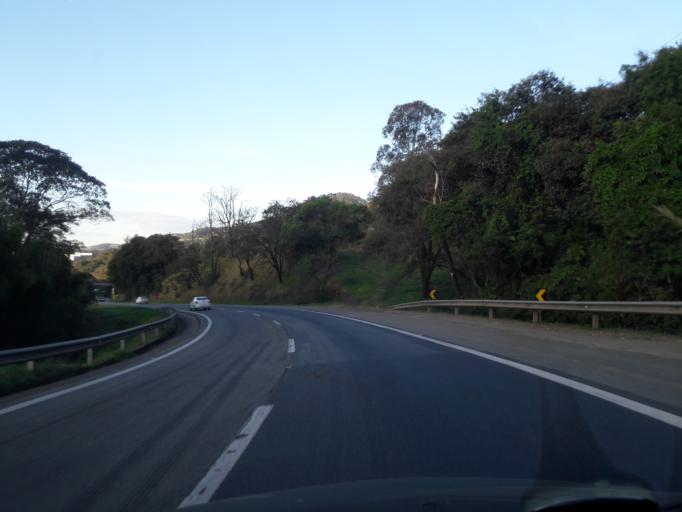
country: BR
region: Minas Gerais
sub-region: Extrema
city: Extrema
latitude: -22.8088
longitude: -46.2642
